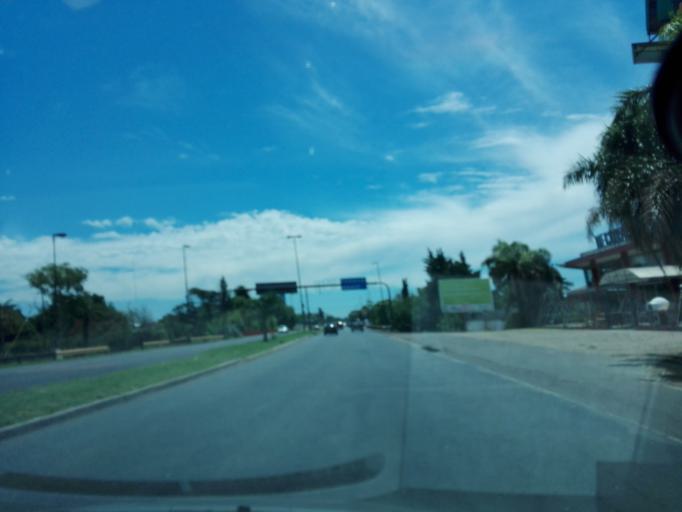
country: AR
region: Buenos Aires
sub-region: Partido de La Plata
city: La Plata
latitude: -34.8923
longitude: -57.9937
